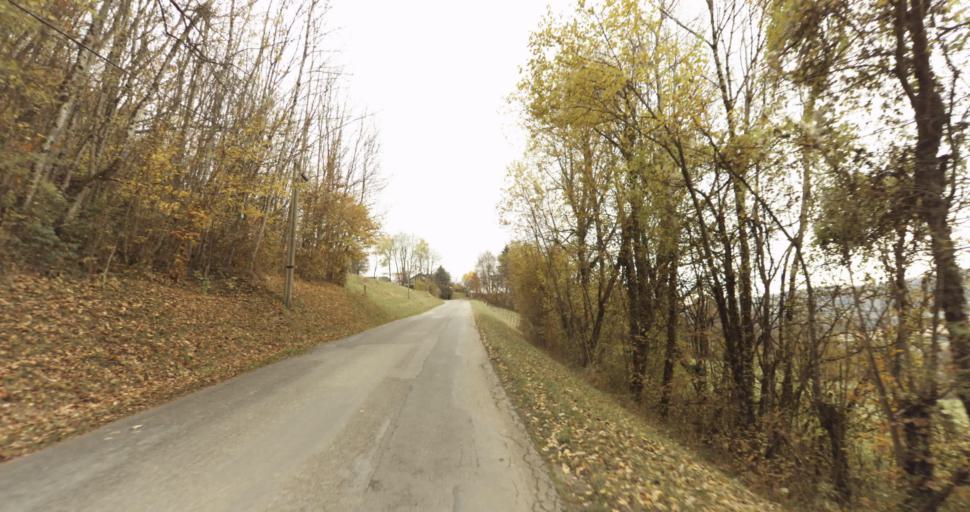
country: FR
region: Rhone-Alpes
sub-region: Departement de la Haute-Savoie
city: Saint-Martin-Bellevue
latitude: 45.9854
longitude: 6.1806
